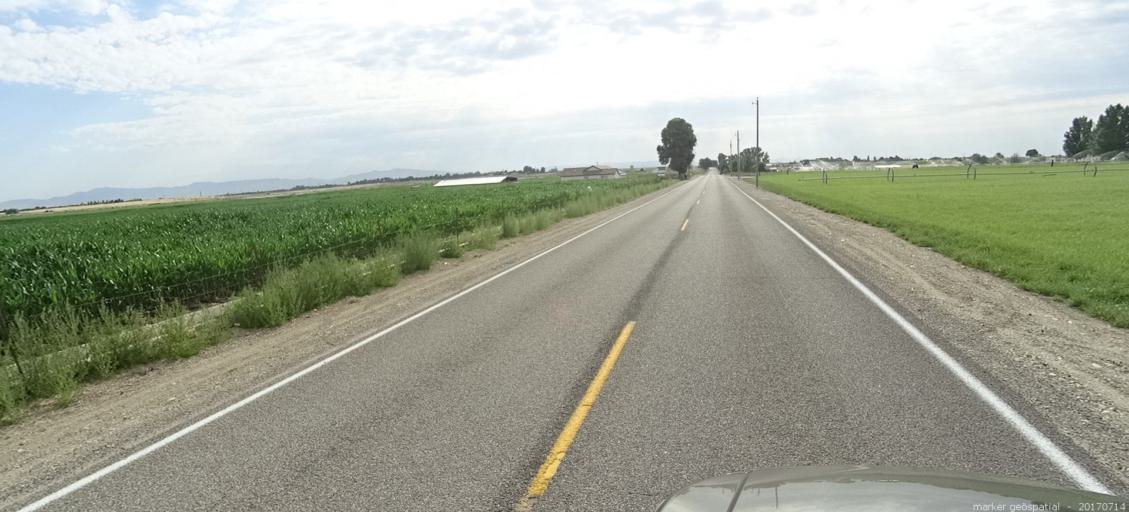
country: US
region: Idaho
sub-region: Ada County
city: Kuna
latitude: 43.4736
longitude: -116.3513
